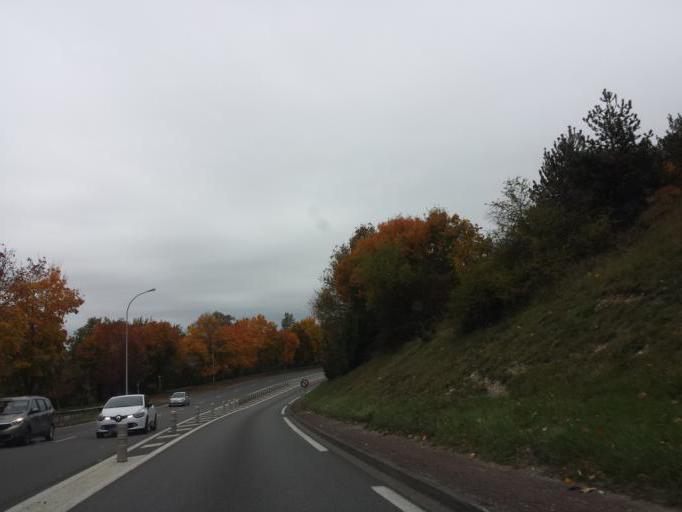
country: FR
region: Poitou-Charentes
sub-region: Departement de la Charente
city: Angouleme
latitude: 45.6303
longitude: 0.1348
